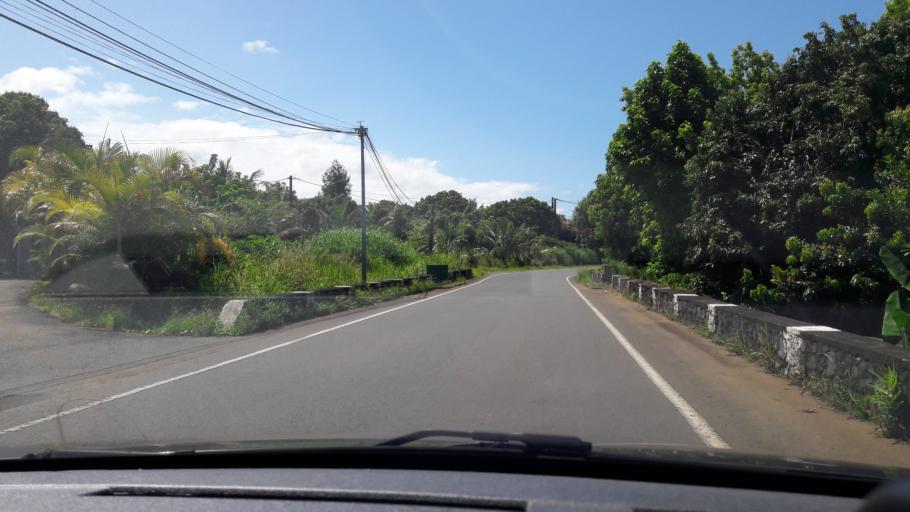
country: RE
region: Reunion
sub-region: Reunion
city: Saint-Benoit
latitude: -21.0895
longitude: 55.7011
